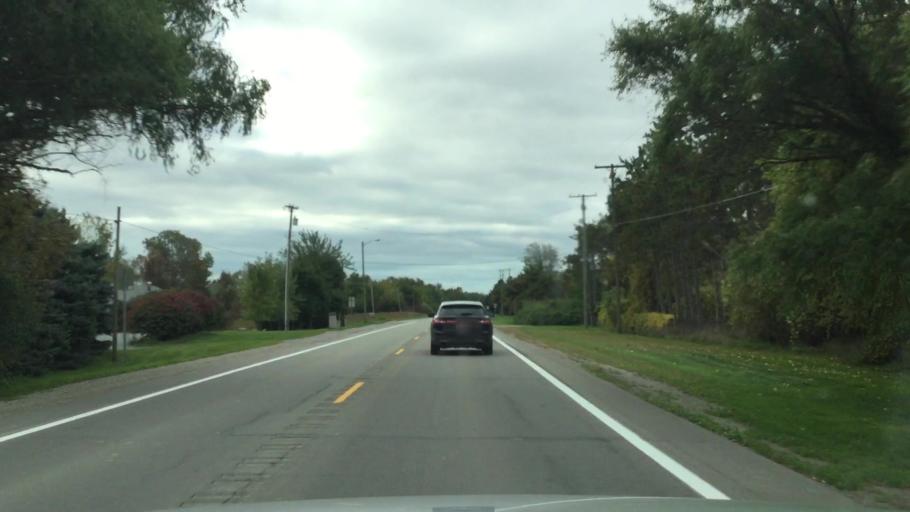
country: US
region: Michigan
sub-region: Macomb County
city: Richmond
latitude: 42.8398
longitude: -82.7617
